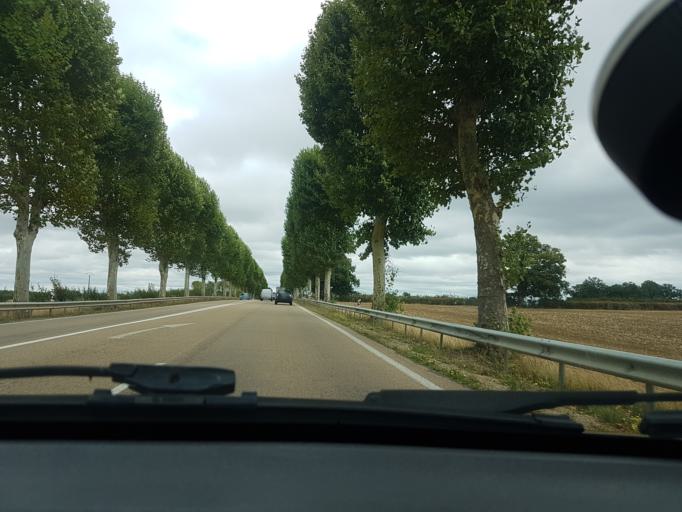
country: FR
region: Bourgogne
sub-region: Departement de l'Yonne
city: Avallon
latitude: 47.4806
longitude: 4.0036
